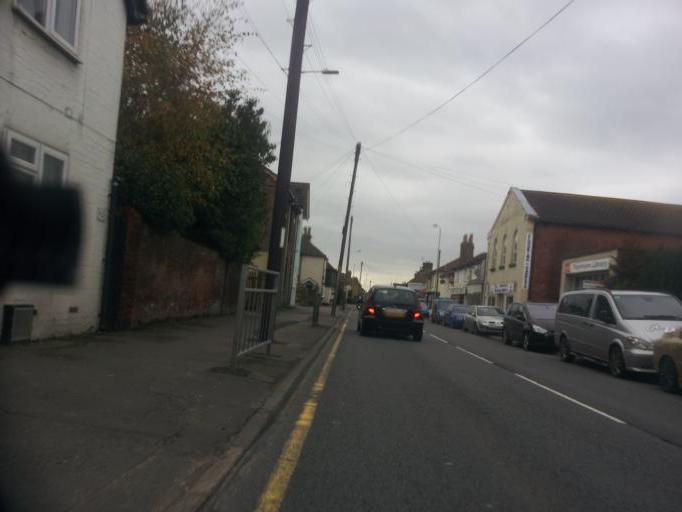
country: GB
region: England
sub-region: Kent
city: Teynham
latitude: 51.3281
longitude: 0.7983
